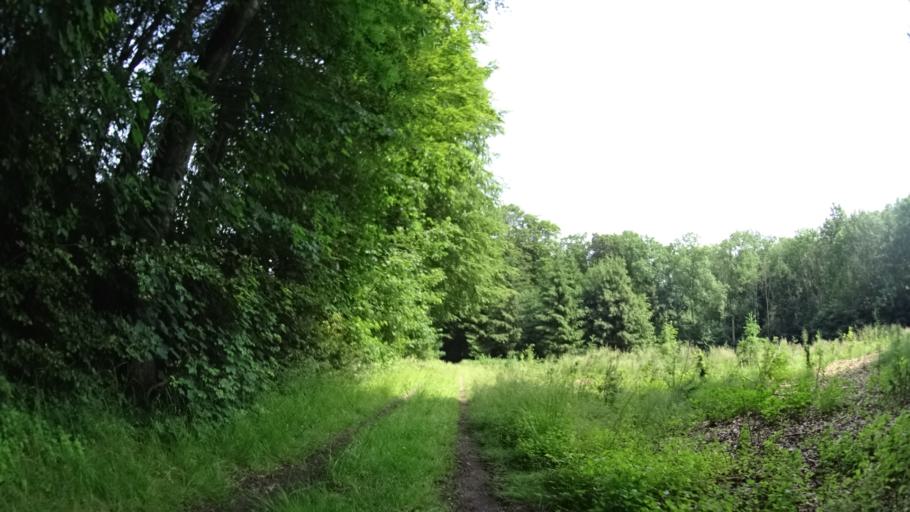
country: DK
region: Central Jutland
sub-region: Arhus Kommune
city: Stavtrup
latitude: 56.1389
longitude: 10.0980
